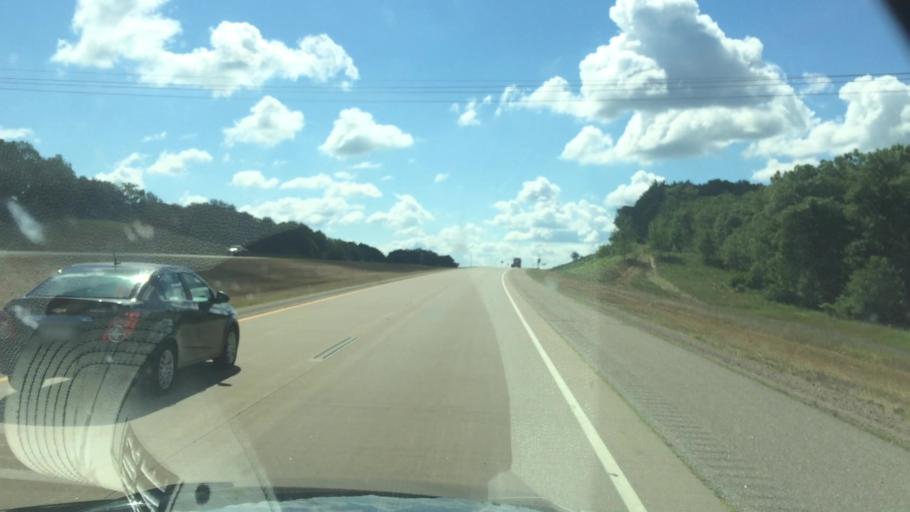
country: US
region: Wisconsin
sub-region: Portage County
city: Amherst
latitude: 44.4179
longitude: -89.2494
